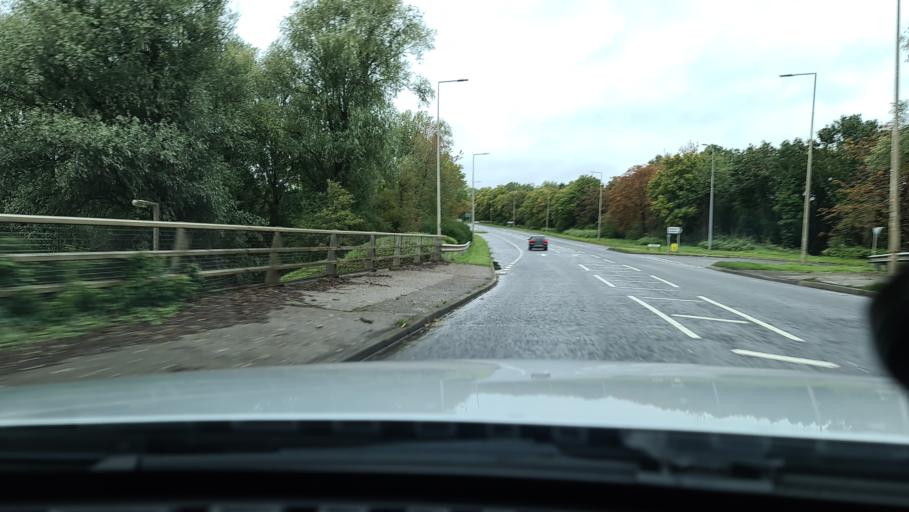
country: GB
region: England
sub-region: Milton Keynes
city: Bradwell
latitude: 52.0497
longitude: -0.8053
